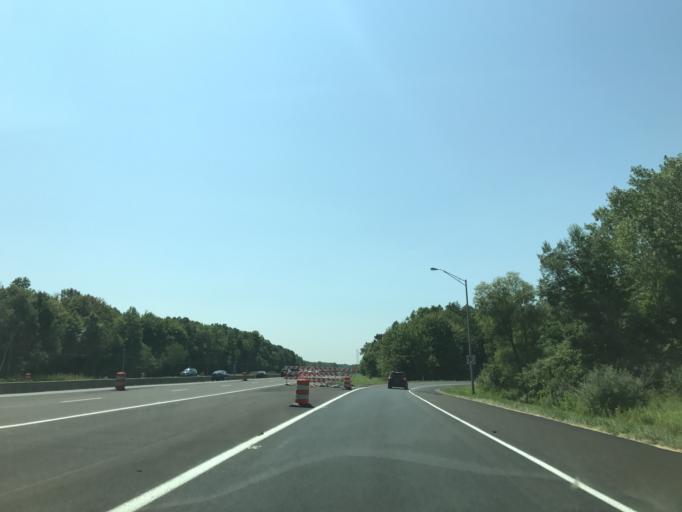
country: US
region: Indiana
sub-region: LaPorte County
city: Long Beach
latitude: 41.7367
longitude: -86.7885
